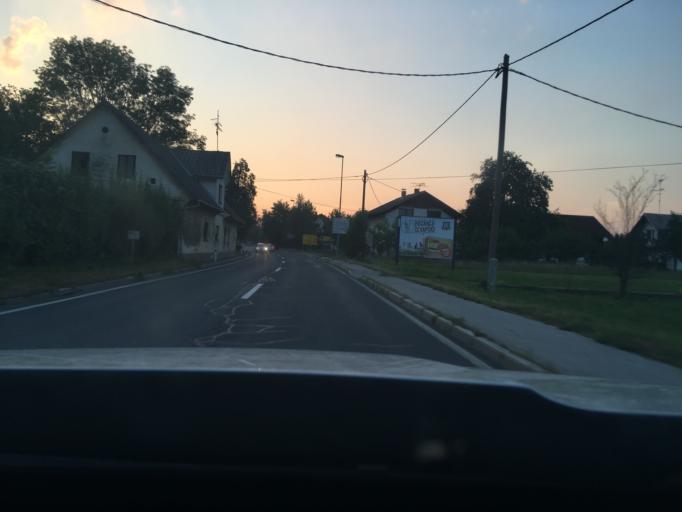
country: SI
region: Ribnica
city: Ribnica
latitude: 45.7330
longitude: 14.7346
